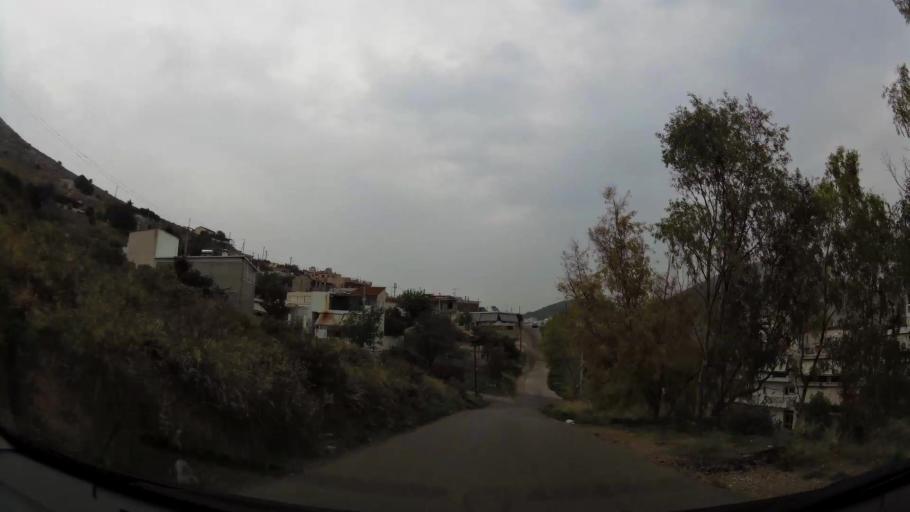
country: GR
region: Attica
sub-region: Nomos Piraios
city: Korydallos
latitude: 37.9914
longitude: 23.6398
